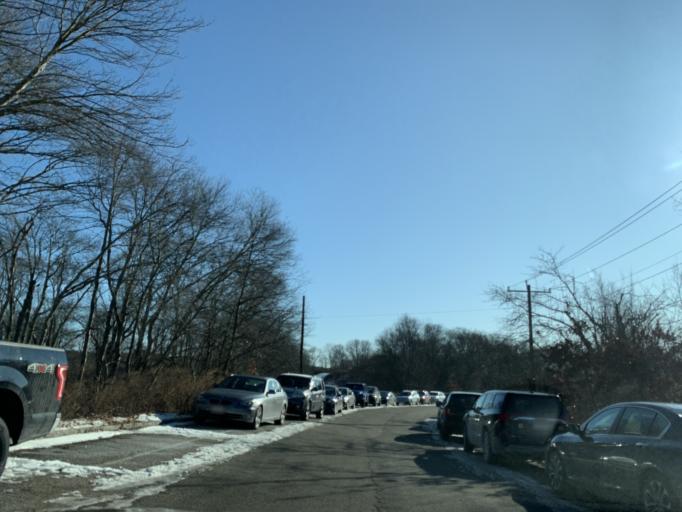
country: US
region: Massachusetts
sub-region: Norfolk County
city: Dedham
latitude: 42.2089
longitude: -71.1452
